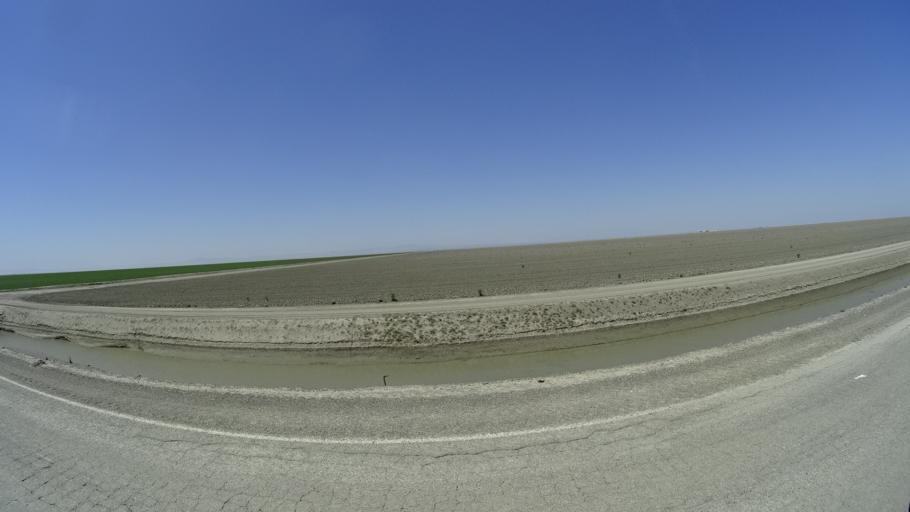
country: US
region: California
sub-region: Kings County
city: Corcoran
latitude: 35.9929
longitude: -119.6432
